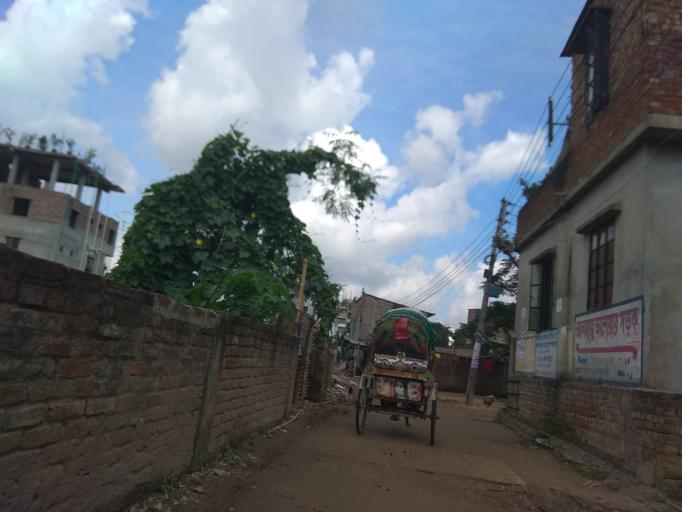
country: BD
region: Dhaka
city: Tungi
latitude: 23.8163
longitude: 90.3898
